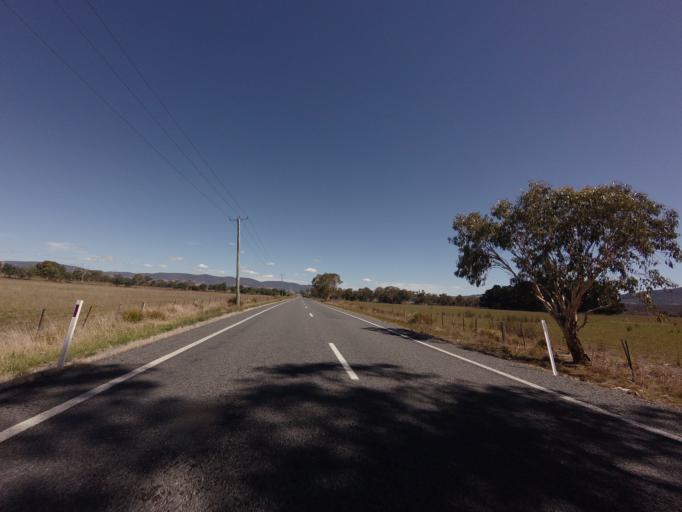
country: AU
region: Tasmania
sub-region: Northern Midlands
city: Evandale
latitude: -41.7650
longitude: 147.7459
